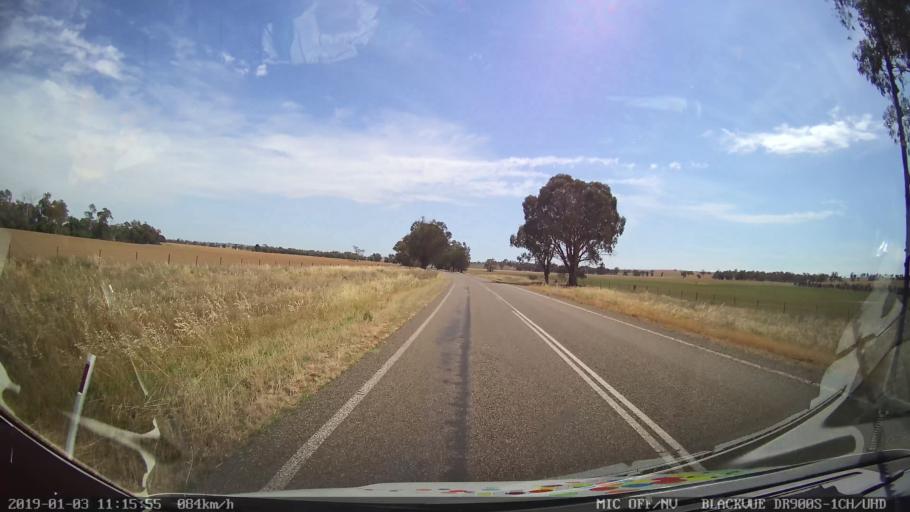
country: AU
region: New South Wales
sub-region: Young
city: Young
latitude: -34.1587
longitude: 148.2683
